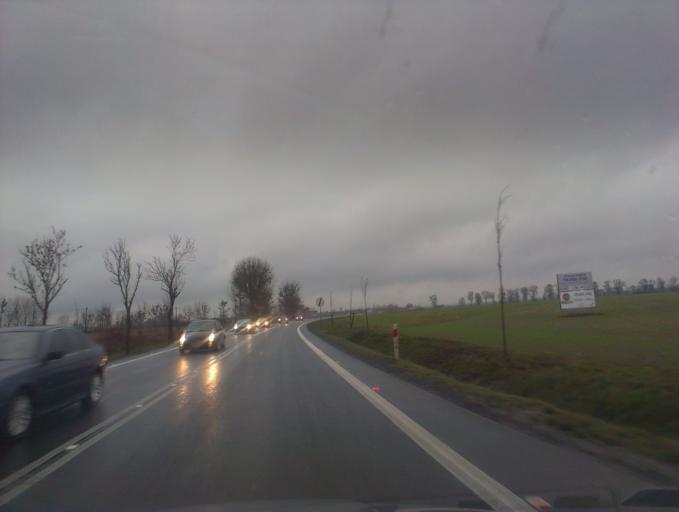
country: PL
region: Greater Poland Voivodeship
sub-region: Powiat obornicki
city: Oborniki
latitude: 52.5945
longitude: 16.8245
